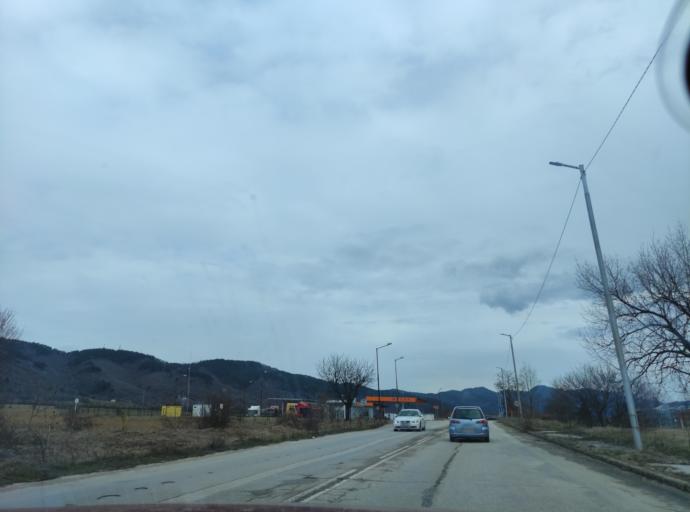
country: BG
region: Sofiya
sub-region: Obshtina Pravets
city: Pravets
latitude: 42.9121
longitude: 23.8834
